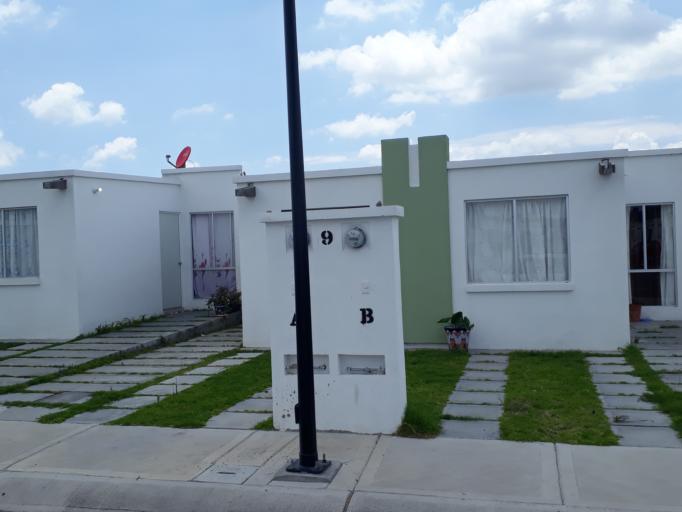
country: MX
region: Aguascalientes
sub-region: Aguascalientes
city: San Sebastian [Fraccionamiento]
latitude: 21.8059
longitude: -102.2738
